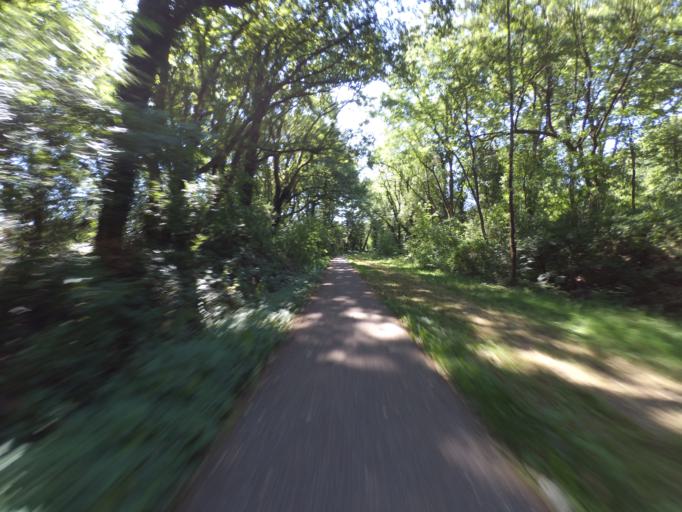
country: NL
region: Drenthe
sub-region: Gemeente Aa en Hunze
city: Anloo
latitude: 52.9400
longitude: 6.6675
